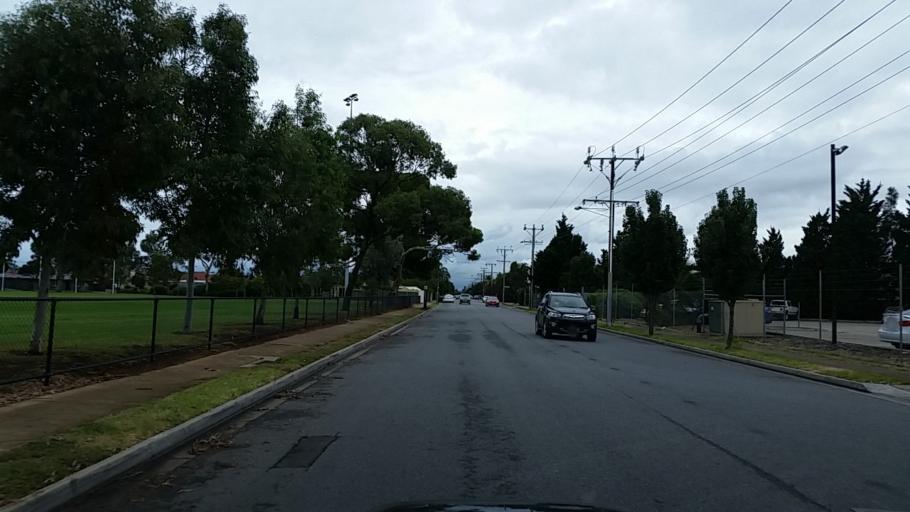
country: AU
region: South Australia
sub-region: Charles Sturt
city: Findon
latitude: -34.8968
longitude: 138.5415
